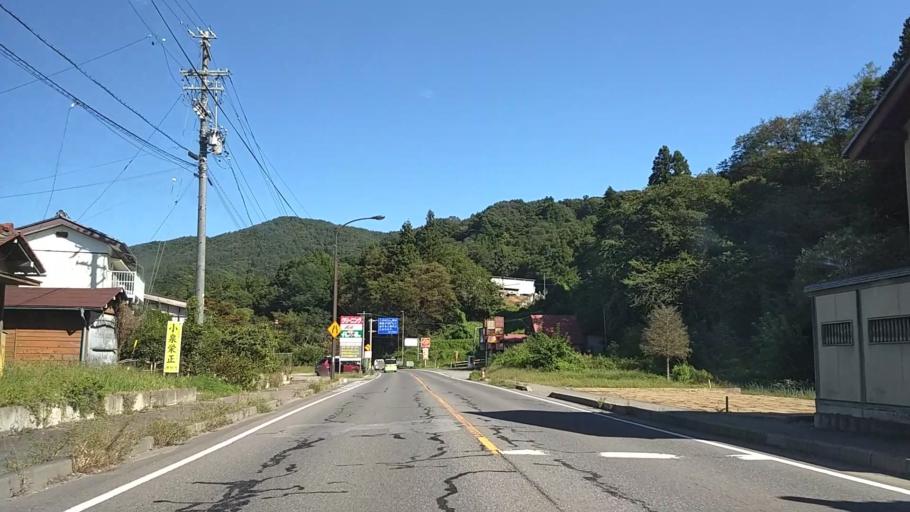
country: JP
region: Nagano
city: Nagano-shi
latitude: 36.6165
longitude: 138.0979
